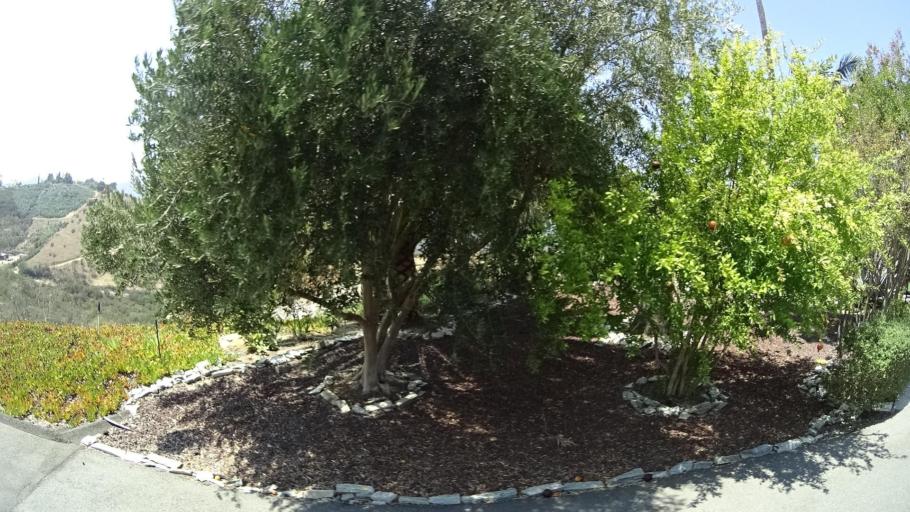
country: US
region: California
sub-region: San Diego County
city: Fallbrook
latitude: 33.4403
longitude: -117.3003
